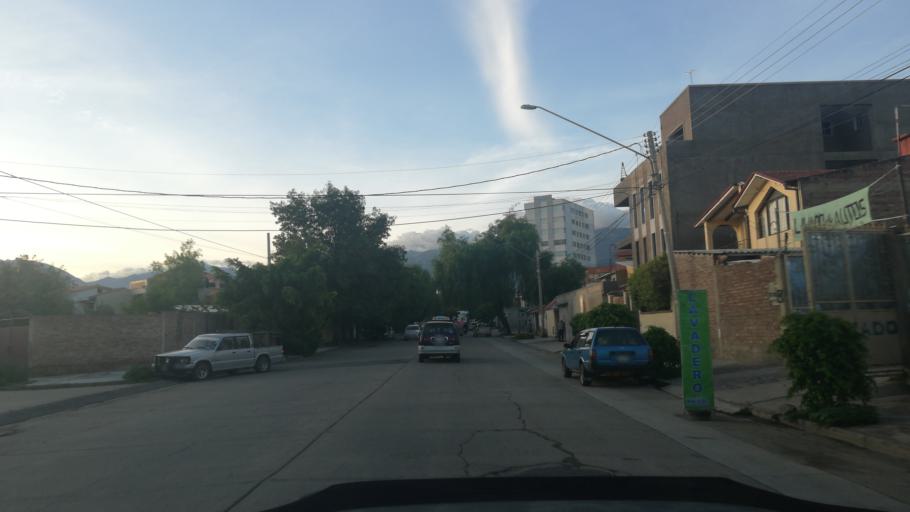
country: BO
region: Cochabamba
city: Cochabamba
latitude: -17.3723
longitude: -66.1878
